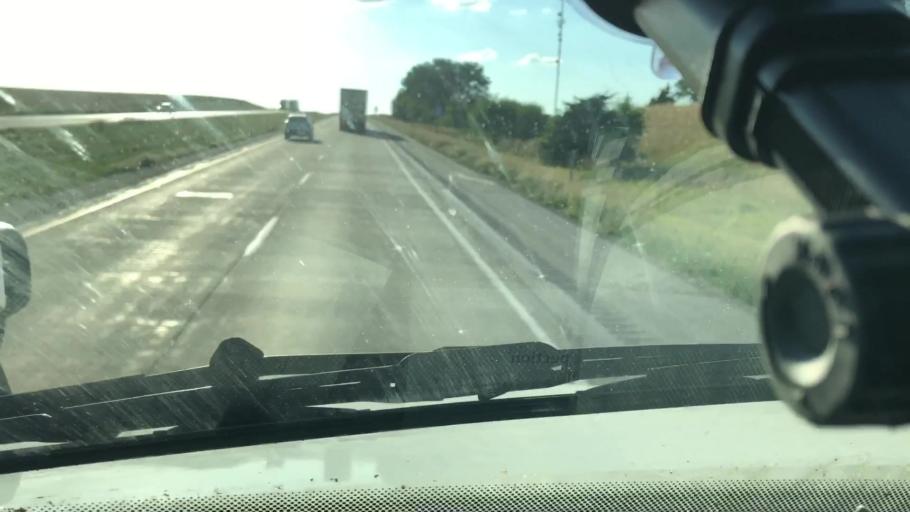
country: US
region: Iowa
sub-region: Pottawattamie County
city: Avoca
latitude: 41.4990
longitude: -95.4591
